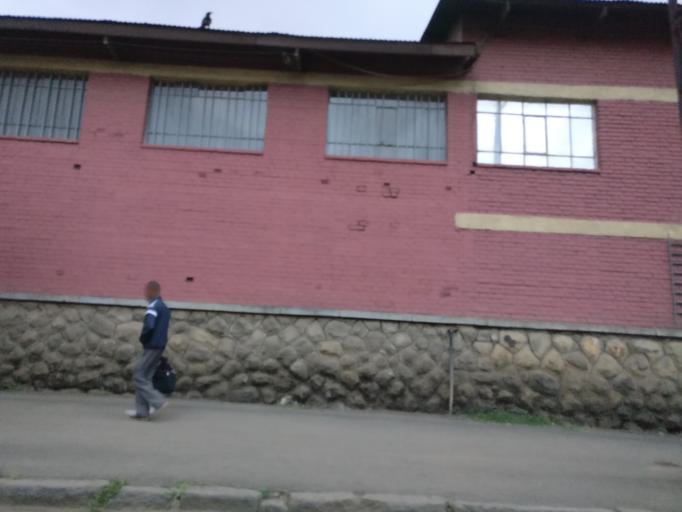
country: ET
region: Adis Abeba
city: Addis Ababa
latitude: 9.0167
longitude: 38.7465
